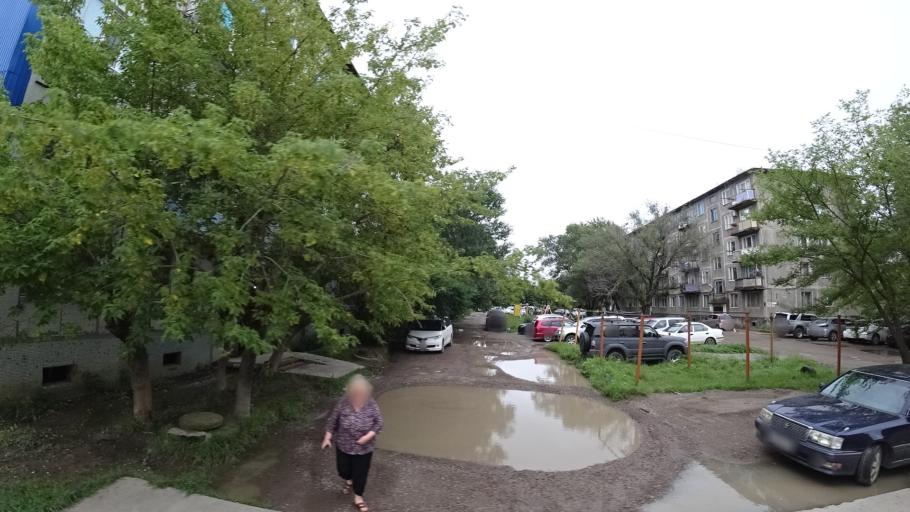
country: RU
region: Primorskiy
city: Chernigovka
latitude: 44.3332
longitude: 132.5378
